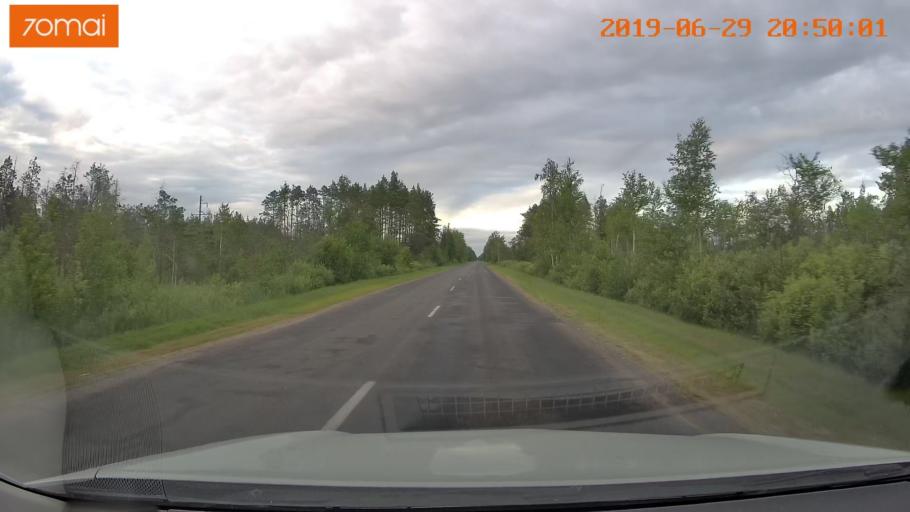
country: BY
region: Brest
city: Hantsavichy
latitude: 52.6717
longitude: 26.3302
